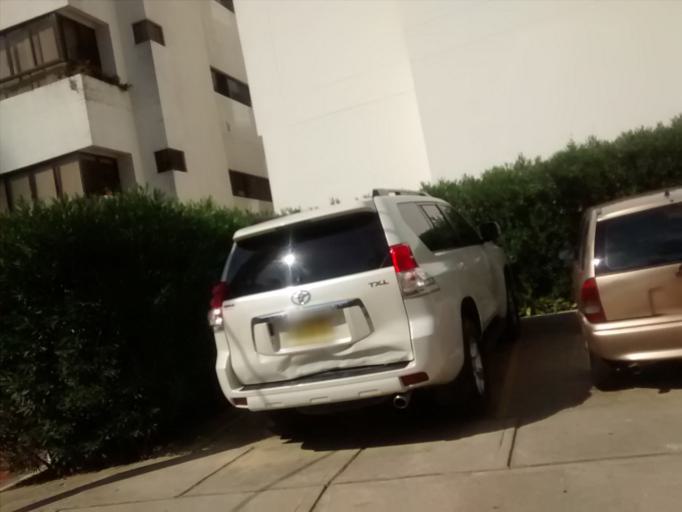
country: CO
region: Bolivar
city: Cartagena
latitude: 10.3924
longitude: -75.5480
